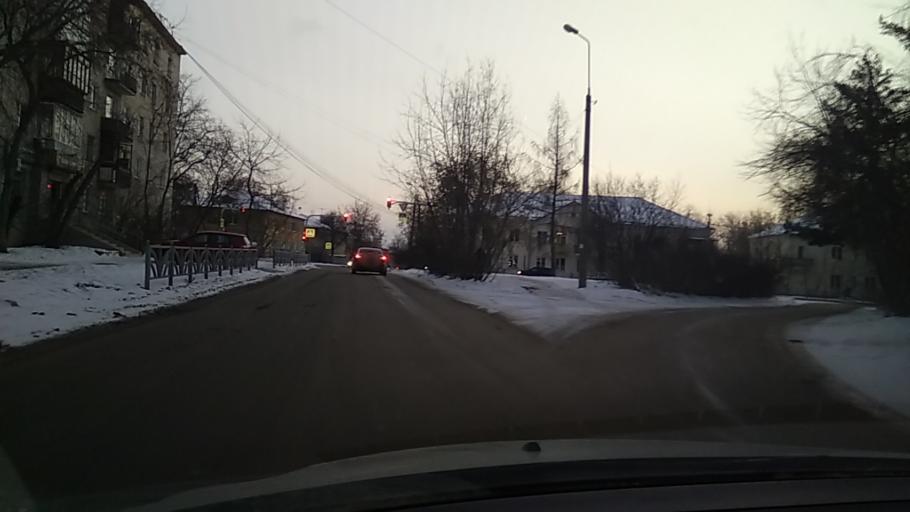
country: RU
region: Sverdlovsk
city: Istok
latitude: 56.7632
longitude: 60.7113
